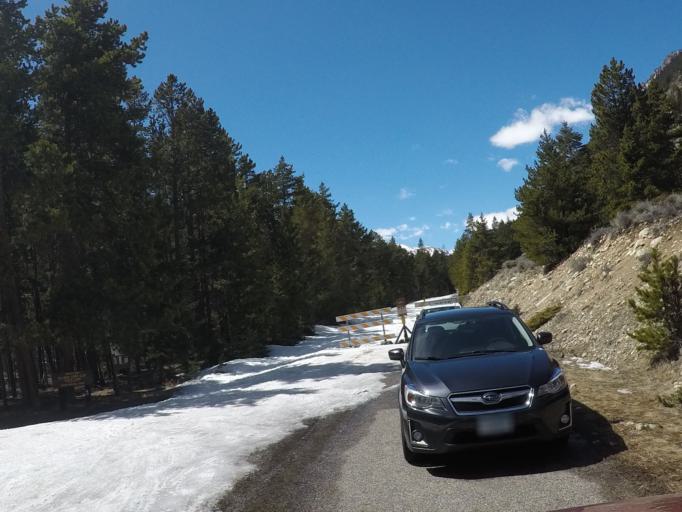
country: US
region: Montana
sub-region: Carbon County
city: Red Lodge
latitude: 45.0813
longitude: -109.3848
